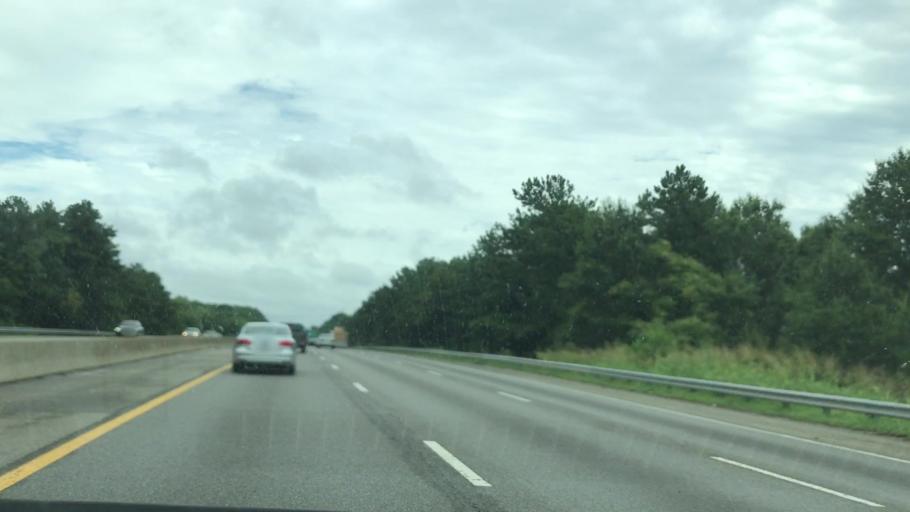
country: US
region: Virginia
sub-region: Chesterfield County
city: Bellwood
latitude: 37.4104
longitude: -77.4262
